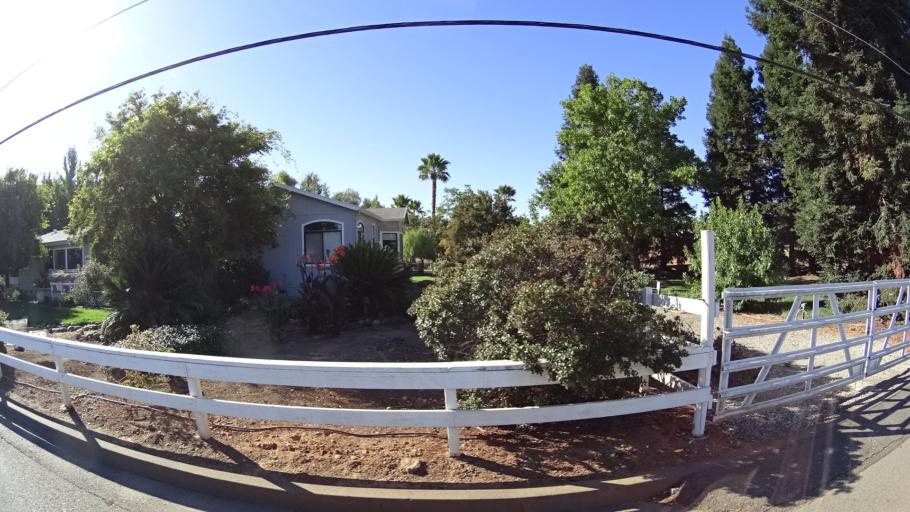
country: US
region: California
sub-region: Sacramento County
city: Vineyard
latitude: 38.4490
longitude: -121.3650
